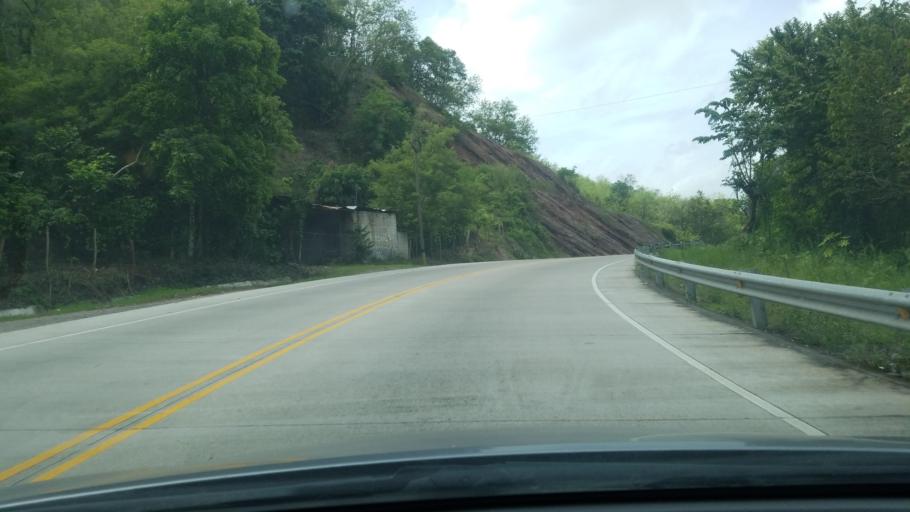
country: HN
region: Copan
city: Veracruz
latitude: 14.9151
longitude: -88.7538
